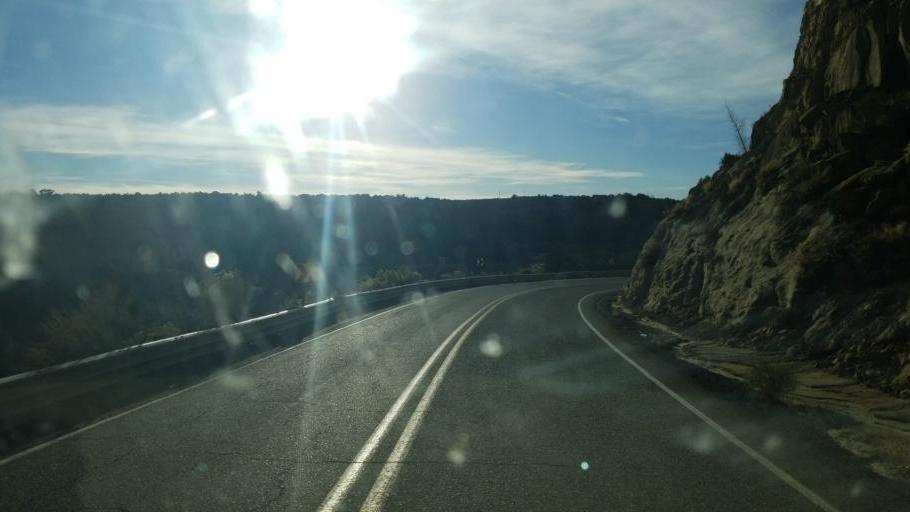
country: US
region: New Mexico
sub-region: San Juan County
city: Bloomfield
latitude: 36.7365
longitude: -107.7010
